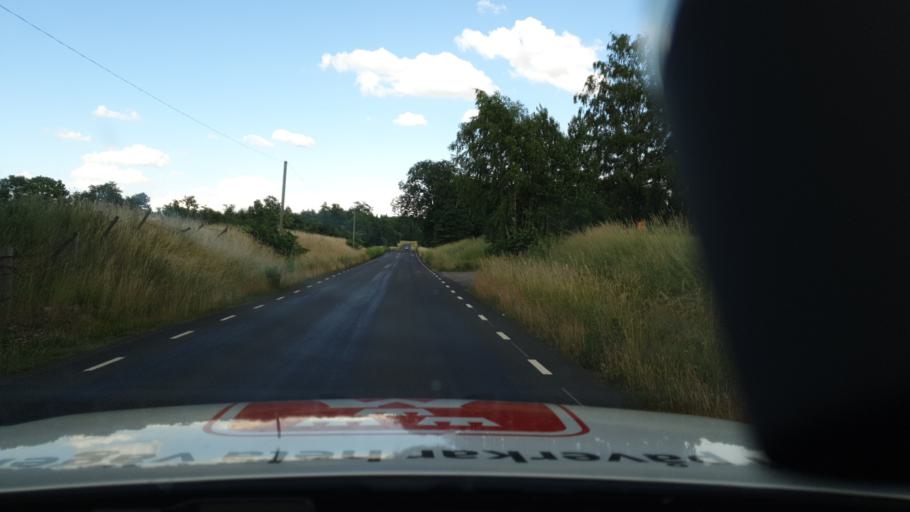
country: SE
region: Vaestra Goetaland
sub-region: Skara Kommun
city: Axvall
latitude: 58.3842
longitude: 13.6033
